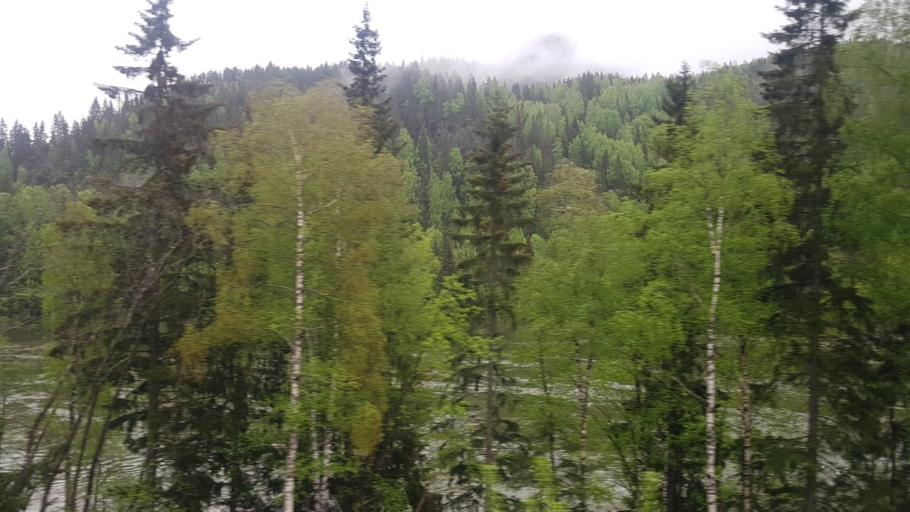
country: NO
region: Oppland
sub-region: Oyer
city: Tretten
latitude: 61.3245
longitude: 10.2931
